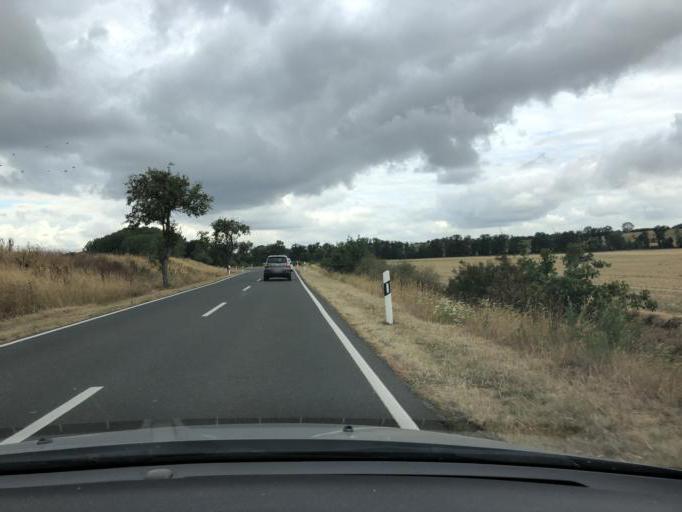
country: DE
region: Saxony-Anhalt
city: Rassnitz
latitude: 51.3914
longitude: 12.1262
